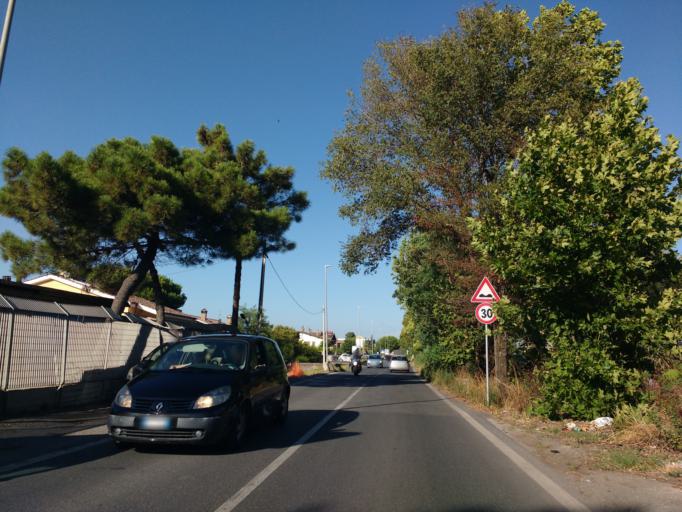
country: IT
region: Latium
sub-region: Citta metropolitana di Roma Capitale
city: Acilia-Castel Fusano-Ostia Antica
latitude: 41.7646
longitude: 12.3116
